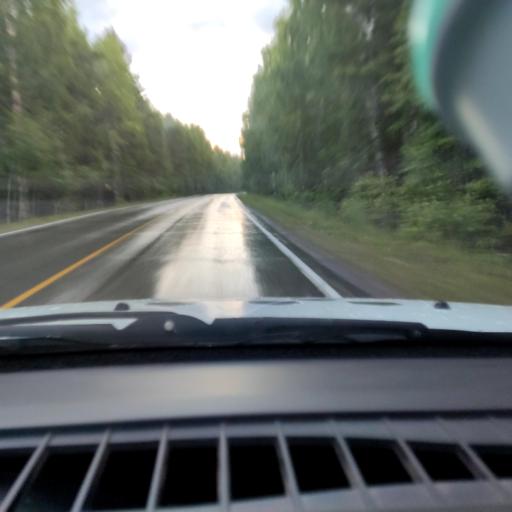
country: RU
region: Chelyabinsk
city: Ozersk
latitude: 55.8351
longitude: 60.6484
